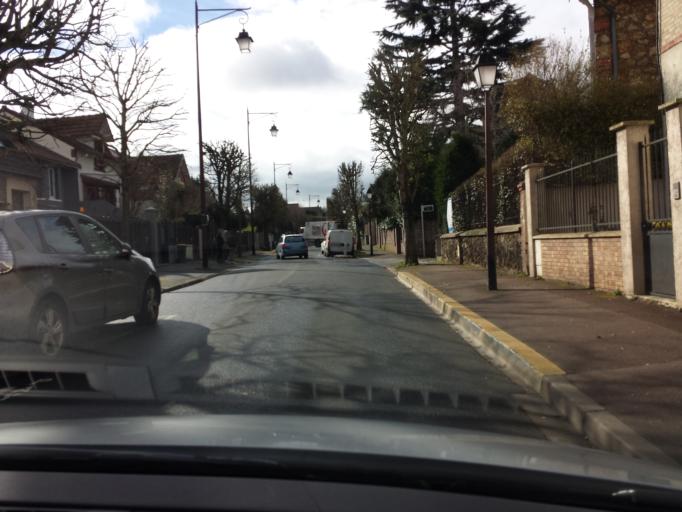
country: FR
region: Ile-de-France
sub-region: Departement des Hauts-de-Seine
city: Antony
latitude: 48.7582
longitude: 2.3000
